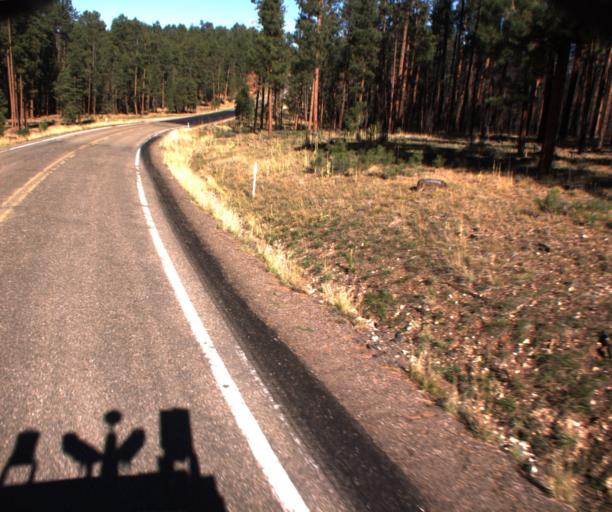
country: US
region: Arizona
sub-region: Coconino County
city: Fredonia
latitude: 36.7361
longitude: -112.2271
